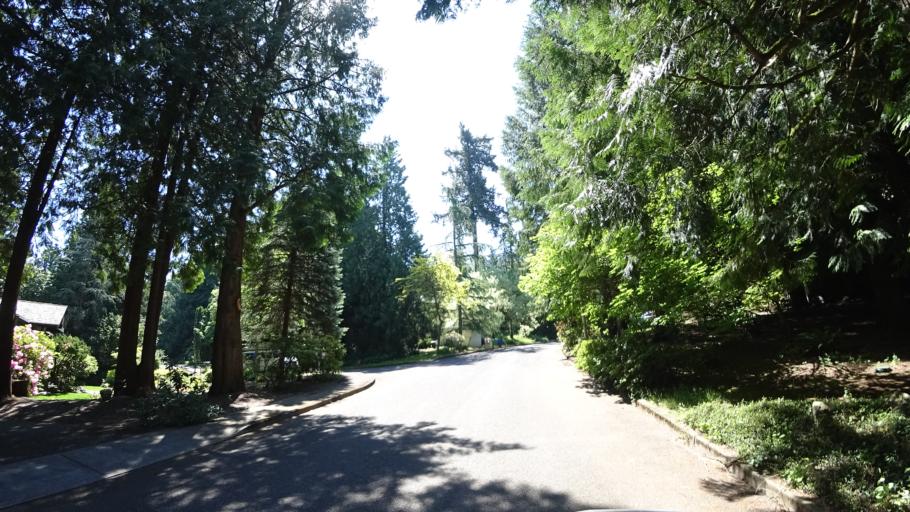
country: US
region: Oregon
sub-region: Clackamas County
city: Happy Valley
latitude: 45.4702
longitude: -122.5267
